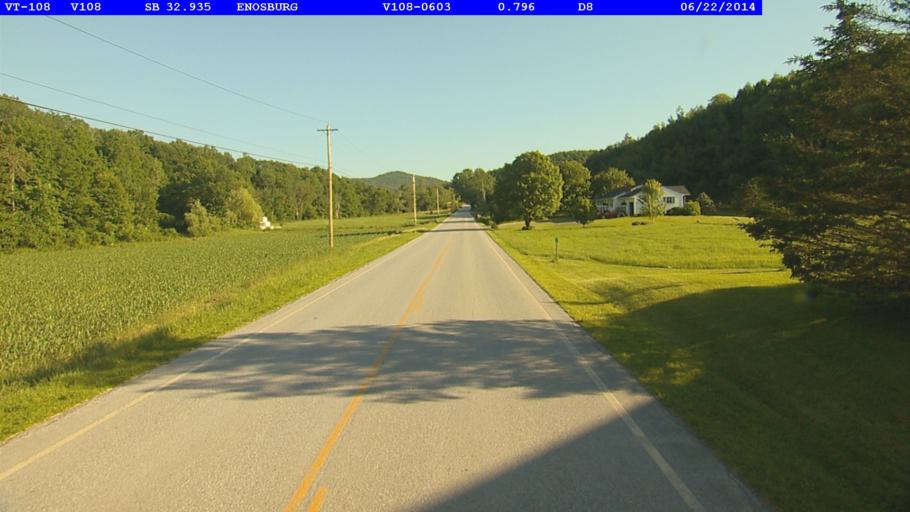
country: US
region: Vermont
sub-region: Franklin County
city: Enosburg Falls
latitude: 44.8495
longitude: -72.8054
